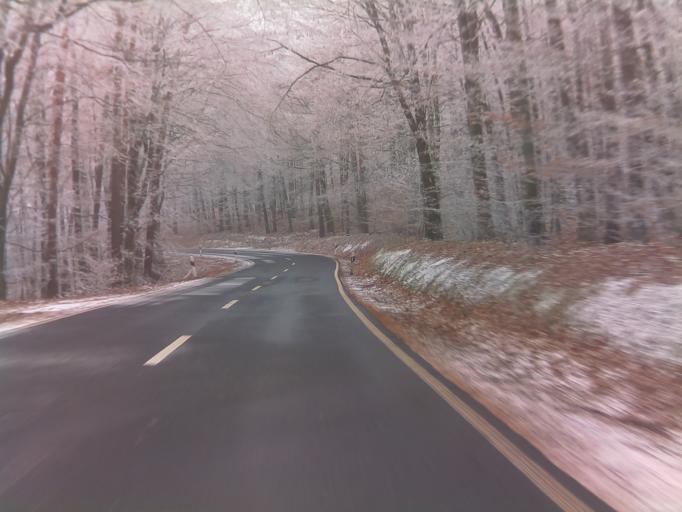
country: DE
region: Bavaria
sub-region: Regierungsbezirk Unterfranken
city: Johannesberg
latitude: 50.0462
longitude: 9.0882
